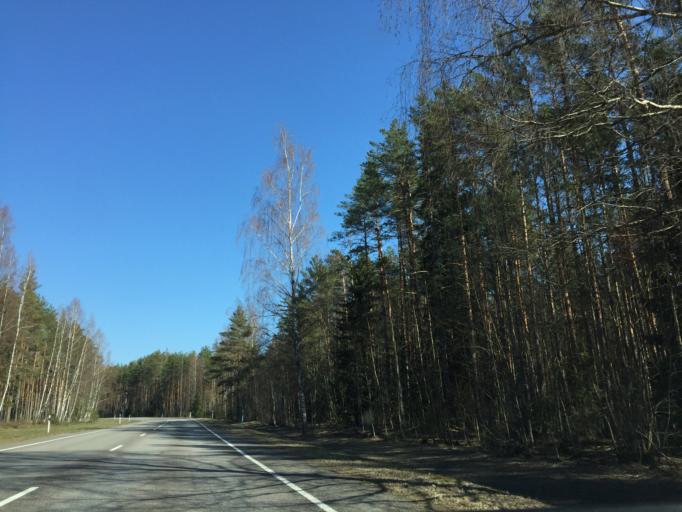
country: EE
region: Jogevamaa
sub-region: Mustvee linn
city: Mustvee
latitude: 58.9923
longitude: 27.1911
